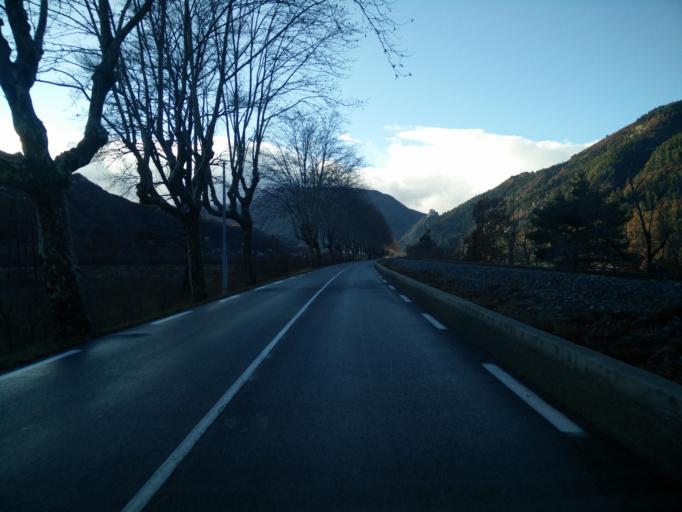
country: FR
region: Provence-Alpes-Cote d'Azur
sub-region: Departement des Alpes-Maritimes
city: Puget-Theniers
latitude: 43.9524
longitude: 6.8415
